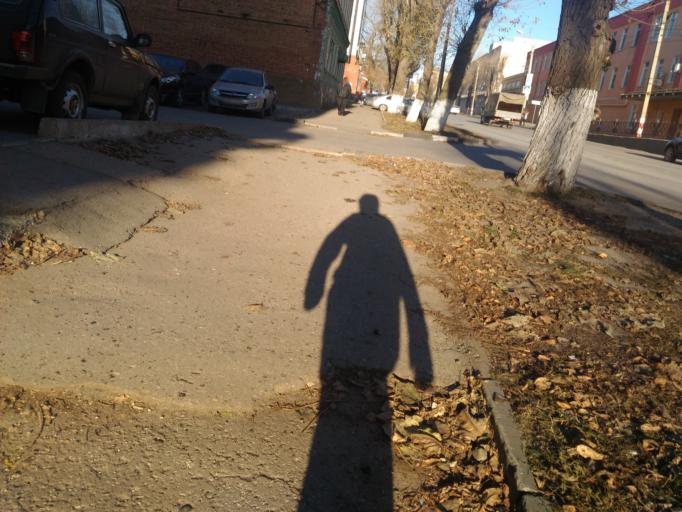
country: RU
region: Ulyanovsk
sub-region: Ulyanovskiy Rayon
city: Ulyanovsk
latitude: 54.3189
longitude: 48.3848
